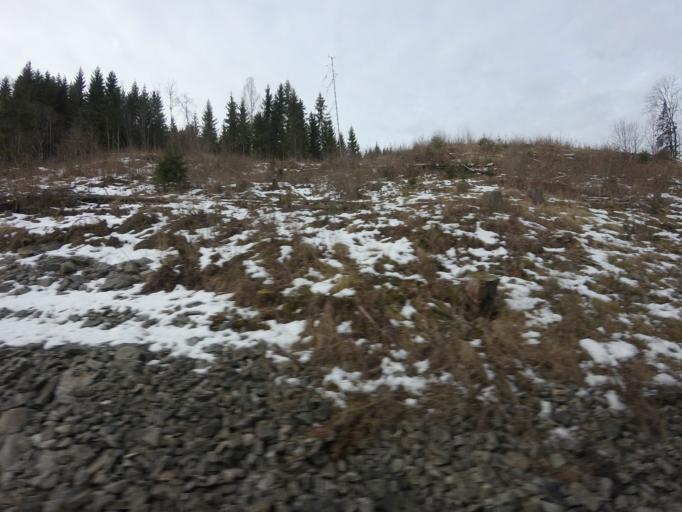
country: NO
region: Akershus
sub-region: Enebakk
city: Flateby
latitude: 59.8435
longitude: 11.2458
